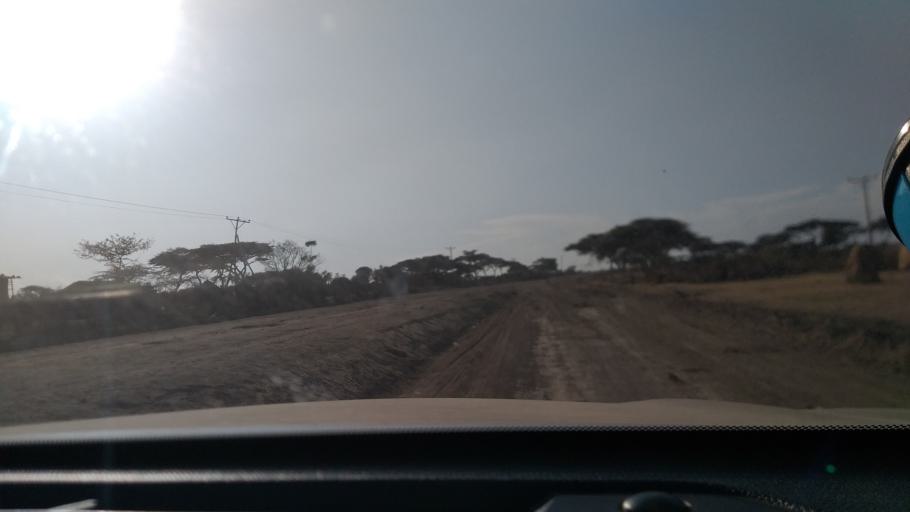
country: ET
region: Oromiya
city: Shashemene
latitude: 7.4972
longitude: 38.7022
